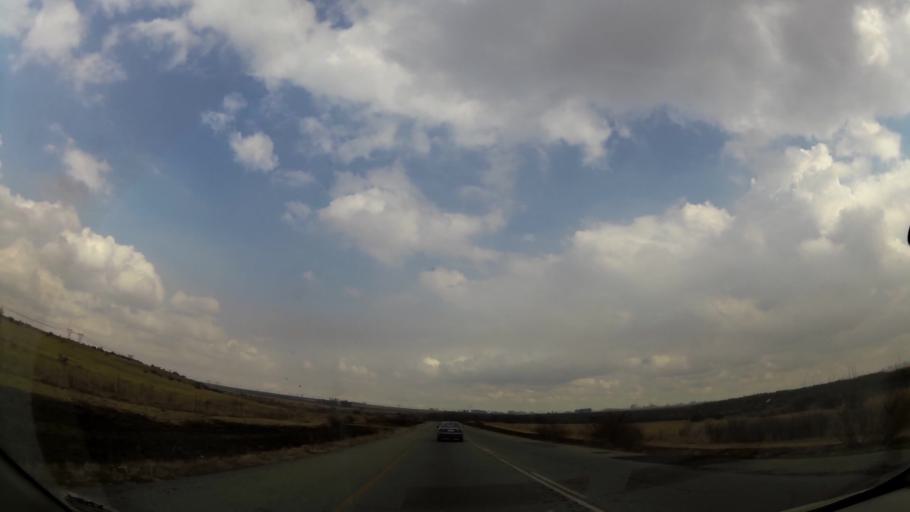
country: ZA
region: Orange Free State
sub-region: Fezile Dabi District Municipality
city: Sasolburg
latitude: -26.7991
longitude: 27.9143
